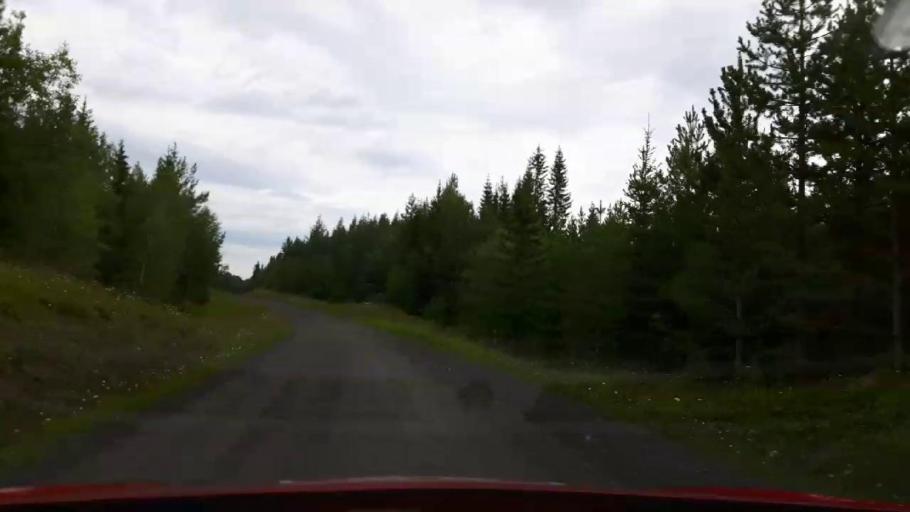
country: SE
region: Jaemtland
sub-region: OEstersunds Kommun
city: Lit
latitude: 63.4010
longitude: 15.2313
